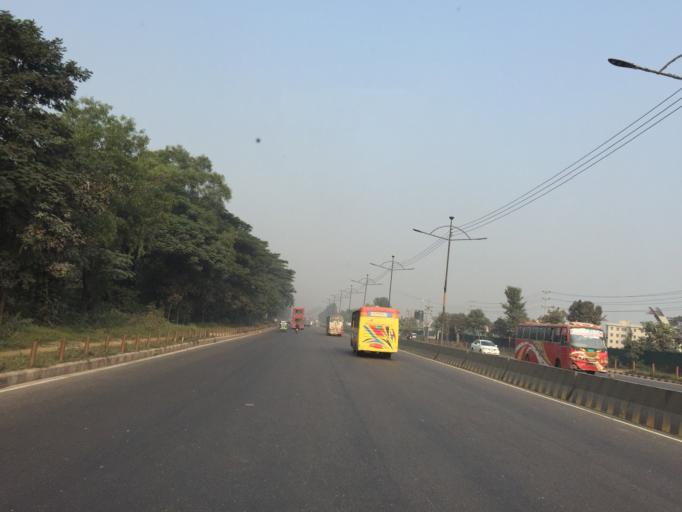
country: BD
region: Dhaka
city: Tungi
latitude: 23.8408
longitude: 90.4164
